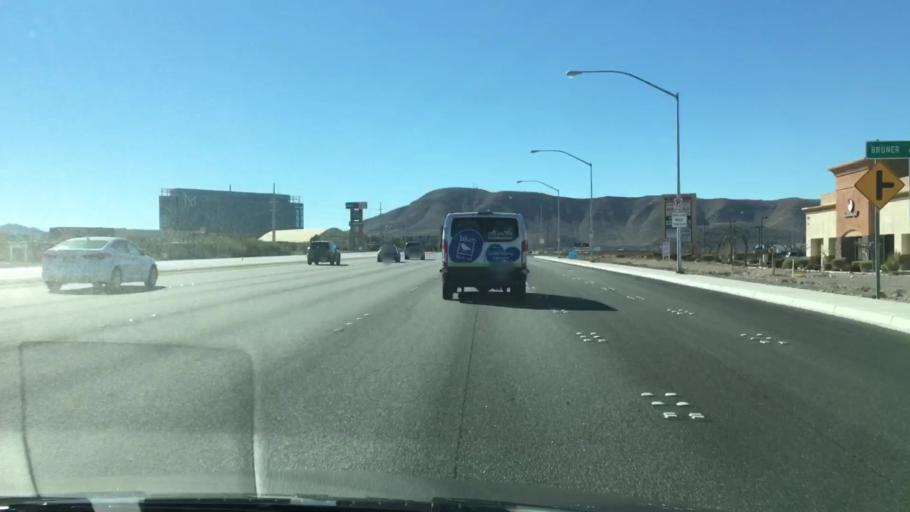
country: US
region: Nevada
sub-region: Clark County
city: Enterprise
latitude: 35.9712
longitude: -115.1652
